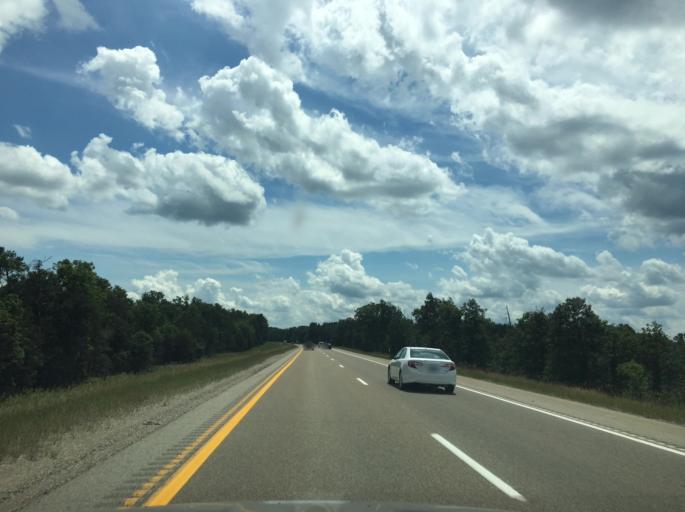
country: US
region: Michigan
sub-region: Crawford County
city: Grayling
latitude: 44.5644
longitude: -84.7082
